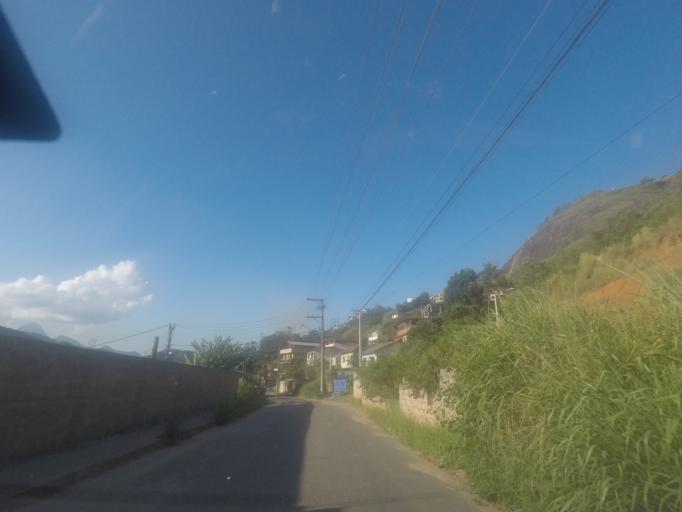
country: BR
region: Rio de Janeiro
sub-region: Petropolis
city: Petropolis
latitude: -22.4907
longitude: -43.1509
